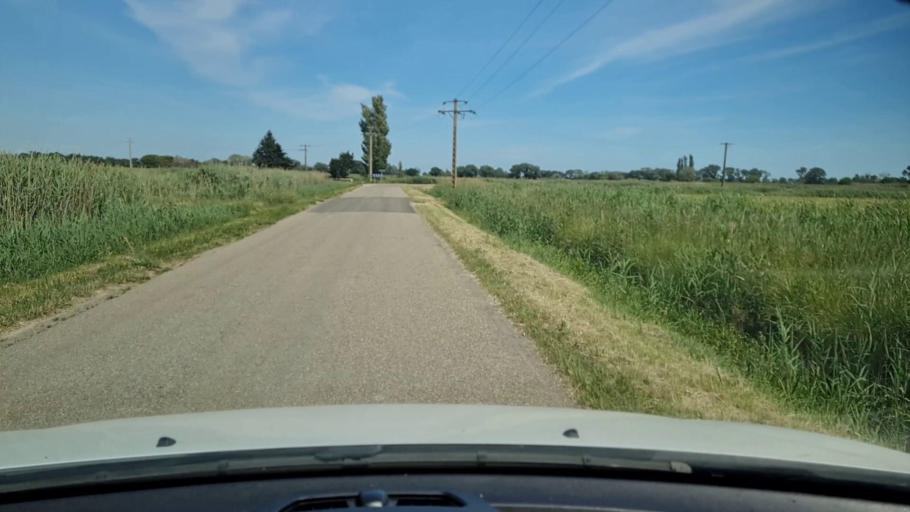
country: FR
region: Languedoc-Roussillon
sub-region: Departement du Gard
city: Saint-Gilles
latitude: 43.6034
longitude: 4.4588
